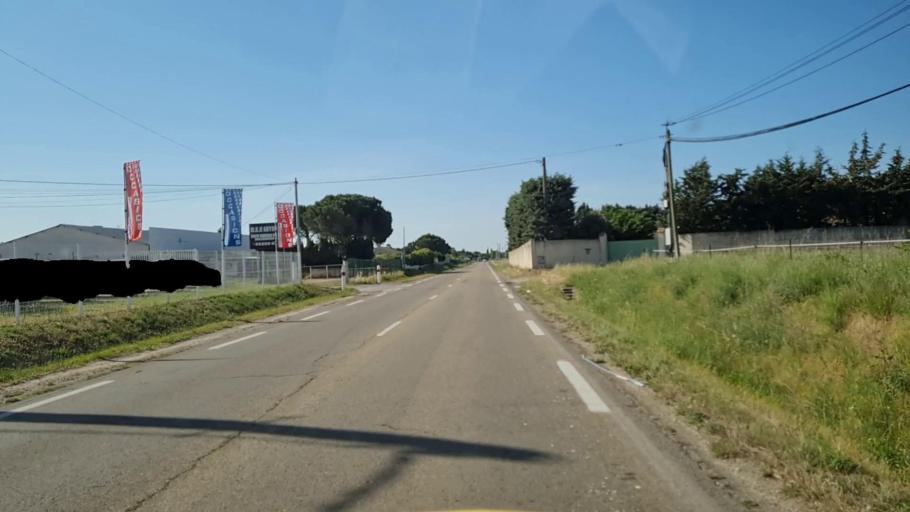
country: FR
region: Languedoc-Roussillon
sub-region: Departement du Gard
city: Saint-Gilles
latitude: 43.6954
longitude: 4.4256
